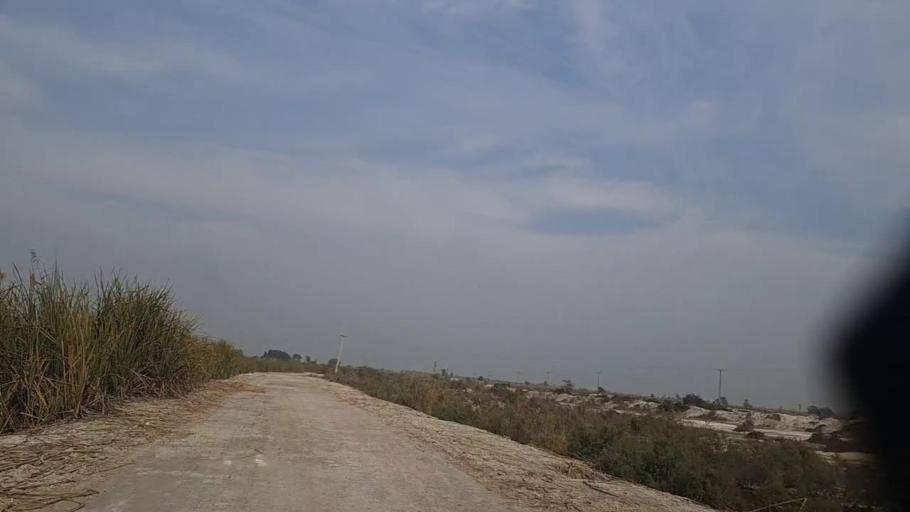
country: PK
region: Sindh
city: Daur
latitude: 26.3693
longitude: 68.2401
